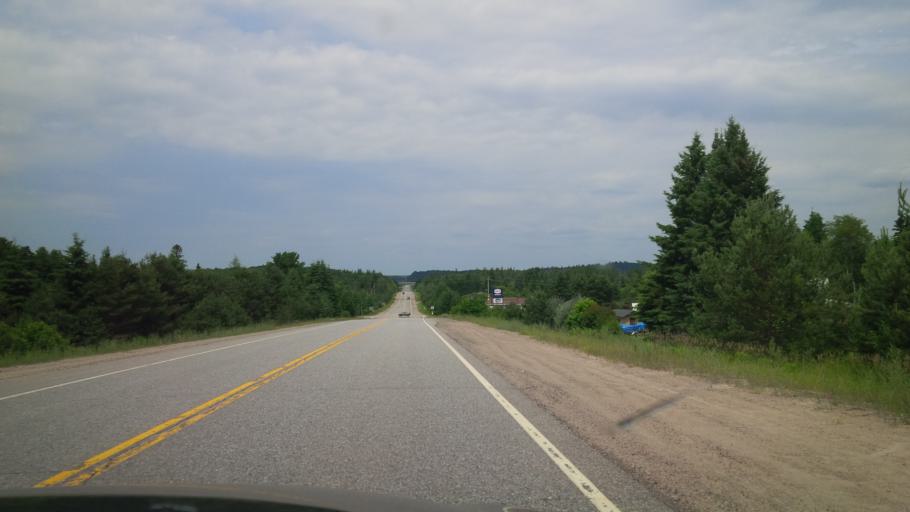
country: CA
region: Ontario
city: Huntsville
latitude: 45.5258
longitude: -79.3187
